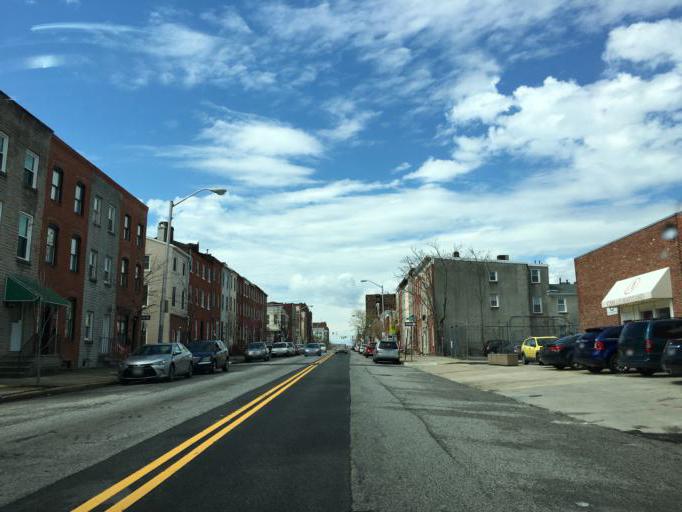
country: US
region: Maryland
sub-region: City of Baltimore
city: Baltimore
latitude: 39.2943
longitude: -76.5851
